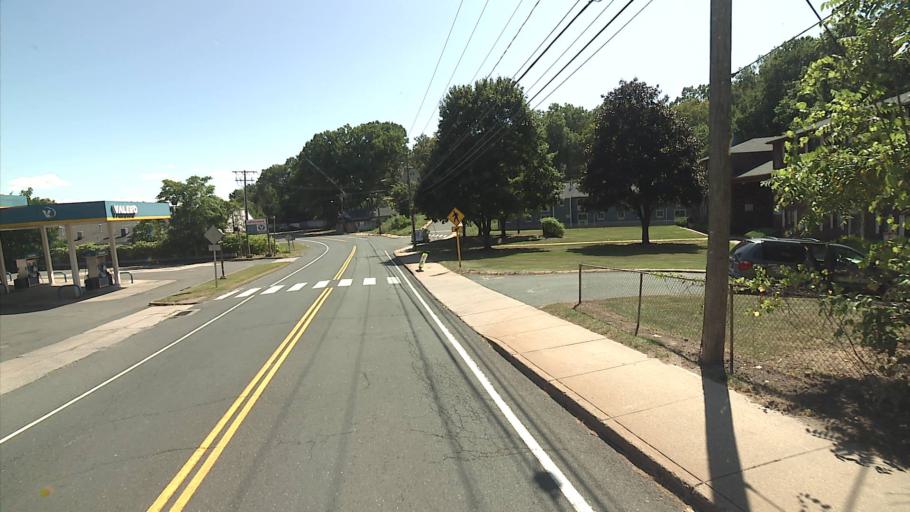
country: US
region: Connecticut
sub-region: Hartford County
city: Windsor Locks
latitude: 41.9349
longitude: -72.6299
